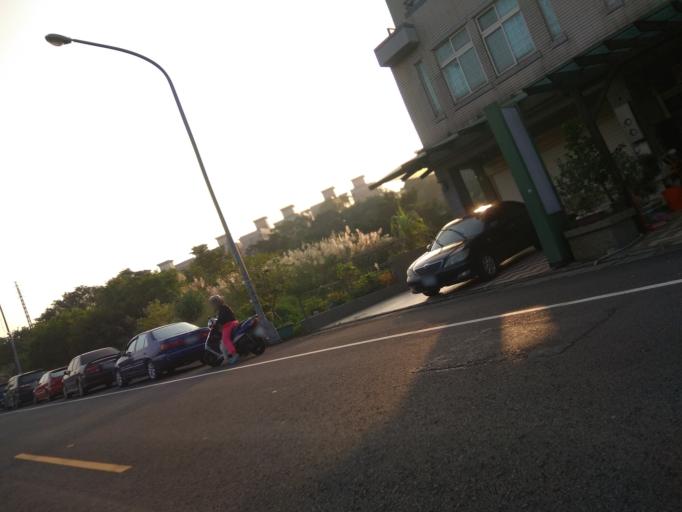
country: TW
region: Taiwan
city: Daxi
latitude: 24.9042
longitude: 121.1774
